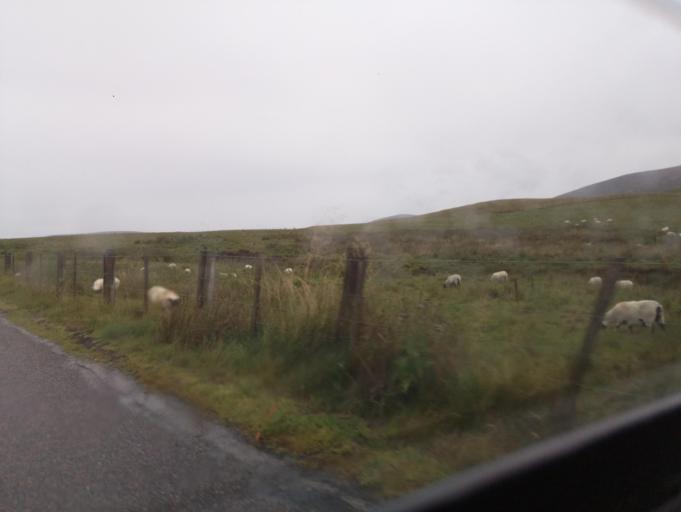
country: GB
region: Scotland
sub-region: Aberdeenshire
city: Ballater
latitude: 57.1644
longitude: -3.2099
